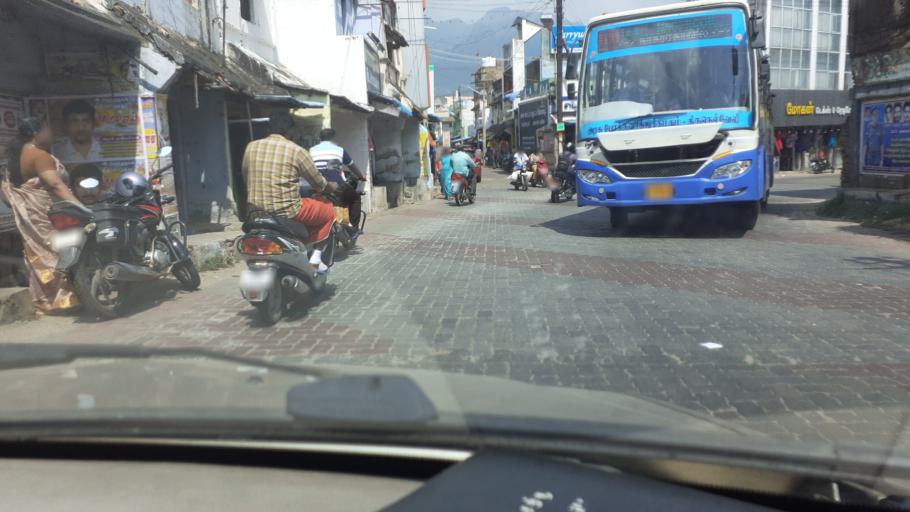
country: IN
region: Tamil Nadu
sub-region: Kanniyakumari
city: Suchindram
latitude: 8.2501
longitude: 77.5214
